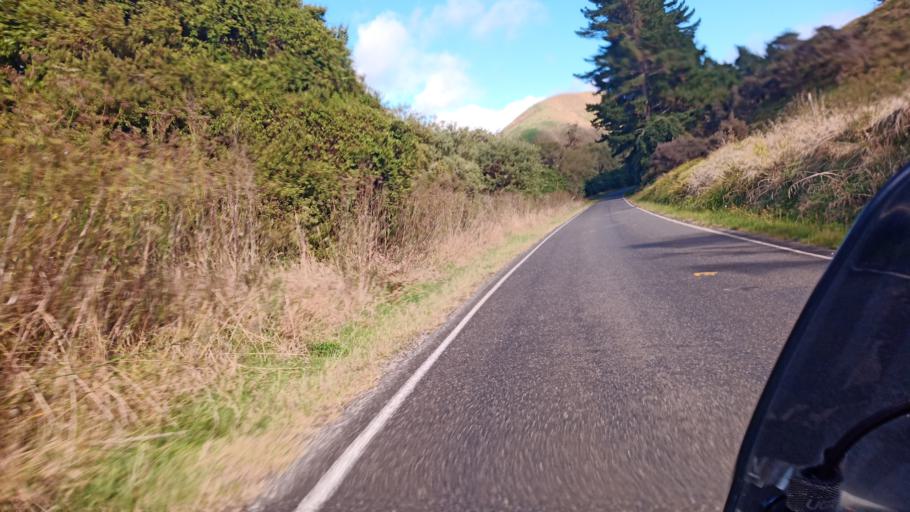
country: NZ
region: Gisborne
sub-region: Gisborne District
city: Gisborne
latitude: -38.5400
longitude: 177.5679
